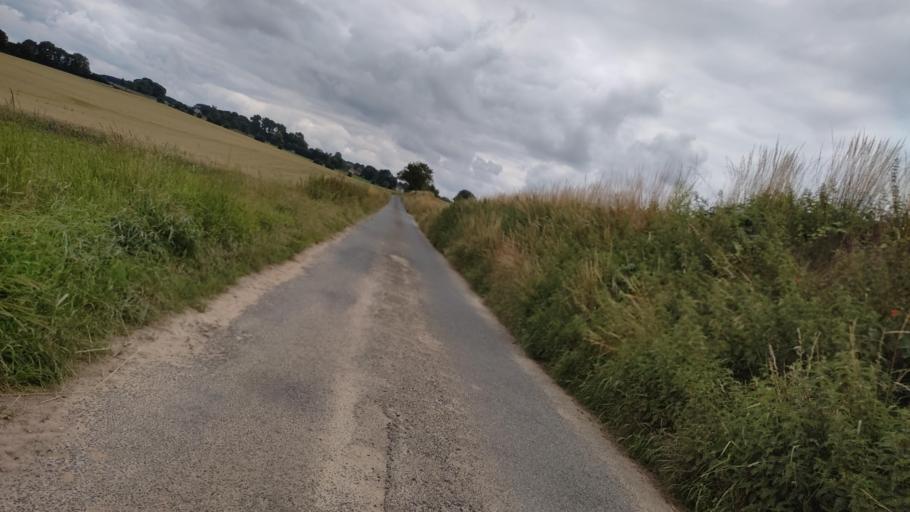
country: FR
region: Nord-Pas-de-Calais
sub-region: Departement du Pas-de-Calais
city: Beaumetz-les-Loges
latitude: 50.2488
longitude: 2.6380
